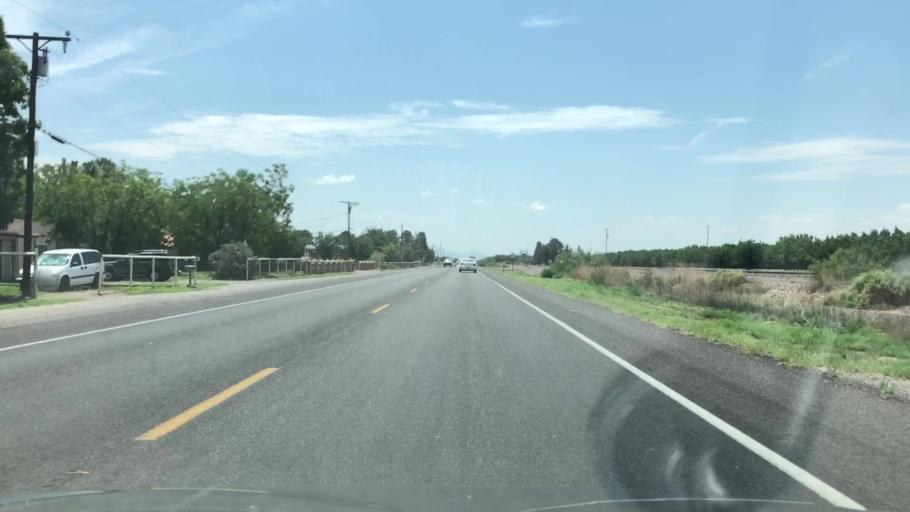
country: US
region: New Mexico
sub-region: Dona Ana County
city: Mesquite
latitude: 32.1819
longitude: -106.7076
